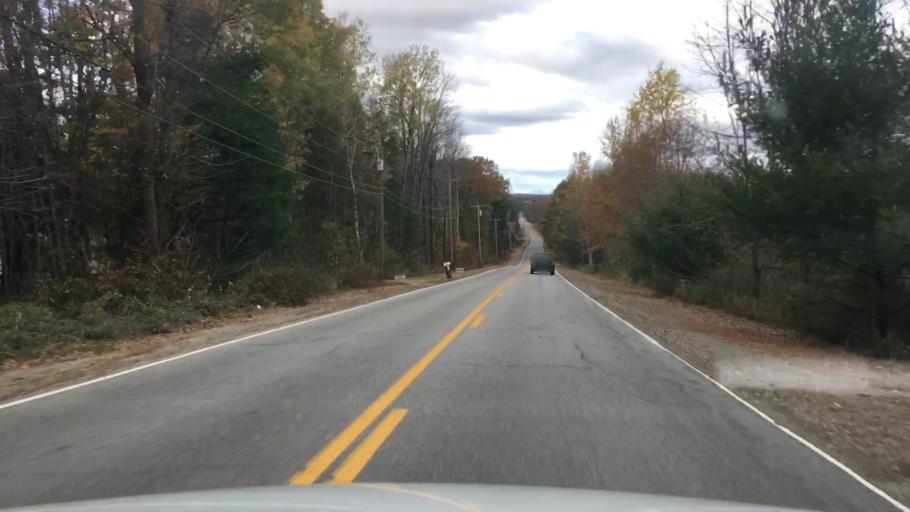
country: US
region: Maine
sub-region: Kennebec County
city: Monmouth
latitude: 44.1875
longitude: -70.0674
